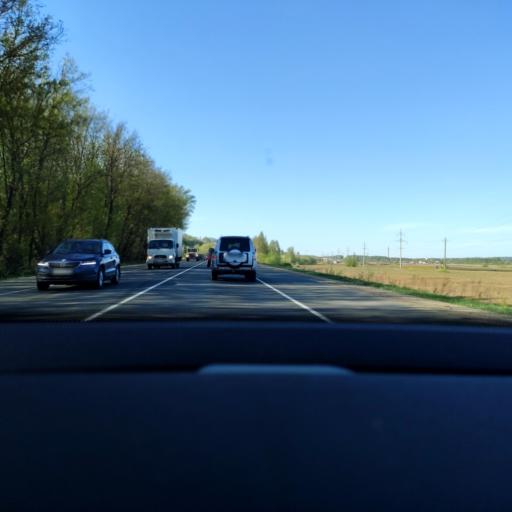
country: RU
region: Moskovskaya
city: Yakhroma
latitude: 56.3294
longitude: 37.4824
